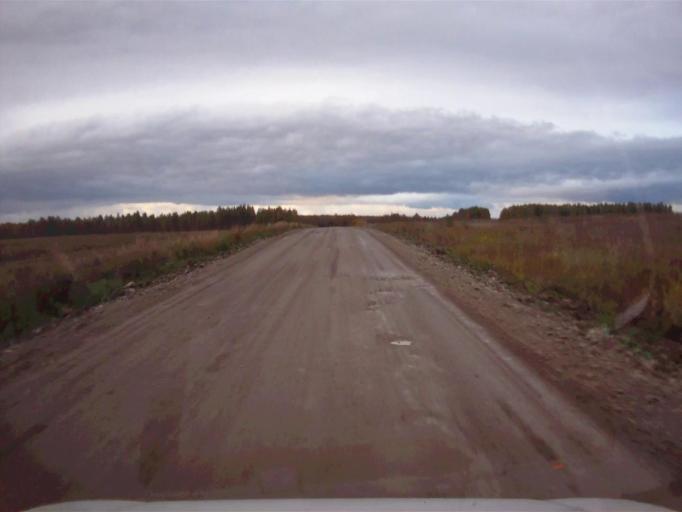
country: RU
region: Sverdlovsk
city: Mikhaylovsk
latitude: 56.1863
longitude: 59.1865
